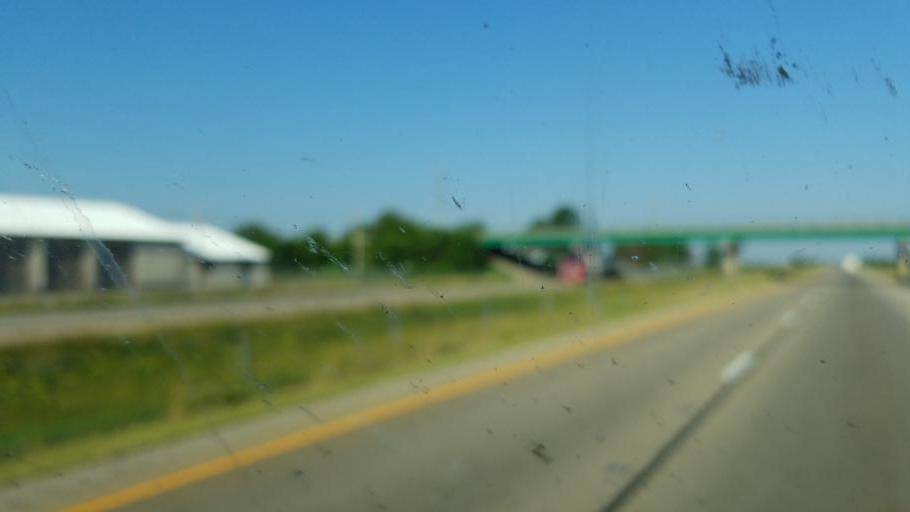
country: US
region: Illinois
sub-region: LaSalle County
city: Ottawa
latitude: 41.3683
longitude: -88.9322
